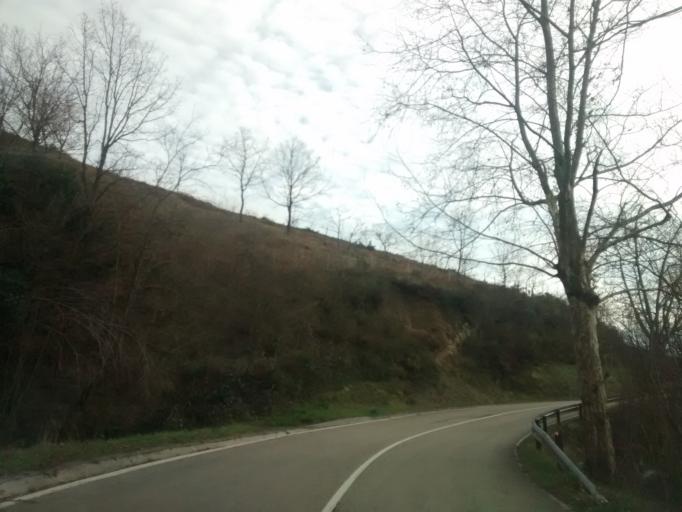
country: ES
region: Cantabria
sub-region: Provincia de Cantabria
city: Ruente
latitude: 43.2458
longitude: -4.3245
